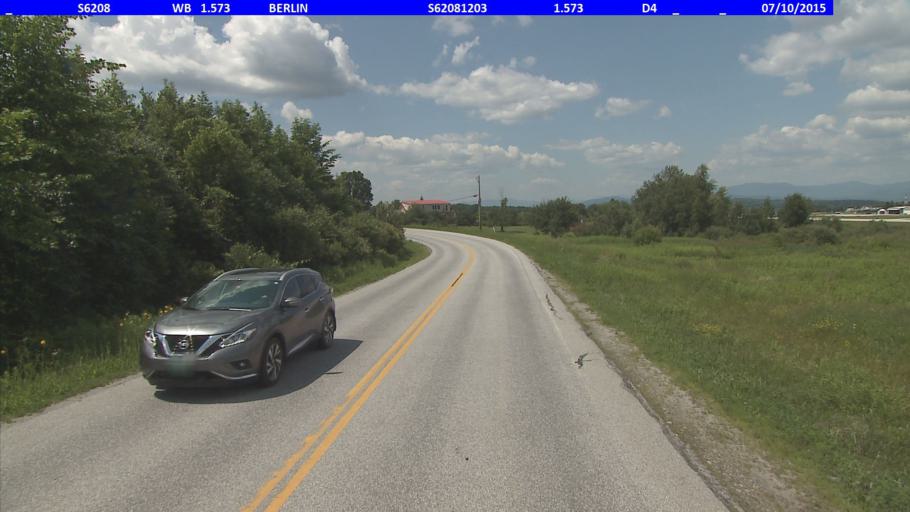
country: US
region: Vermont
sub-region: Washington County
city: South Barre
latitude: 44.1947
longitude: -72.5615
